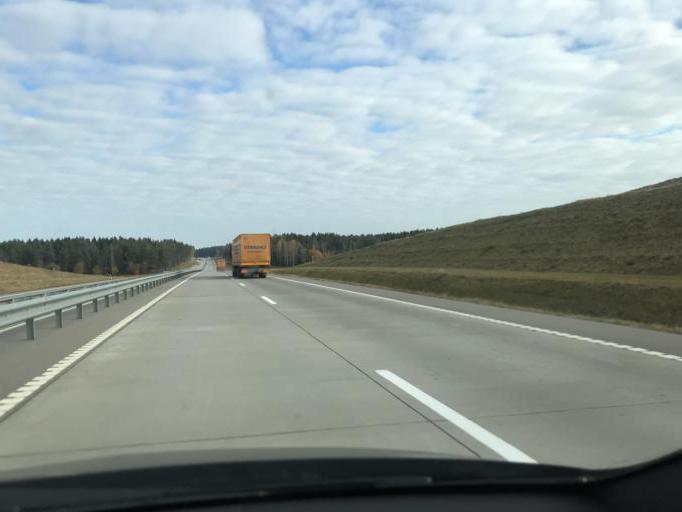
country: BY
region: Minsk
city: Pyatryshki
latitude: 54.0246
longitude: 27.1498
